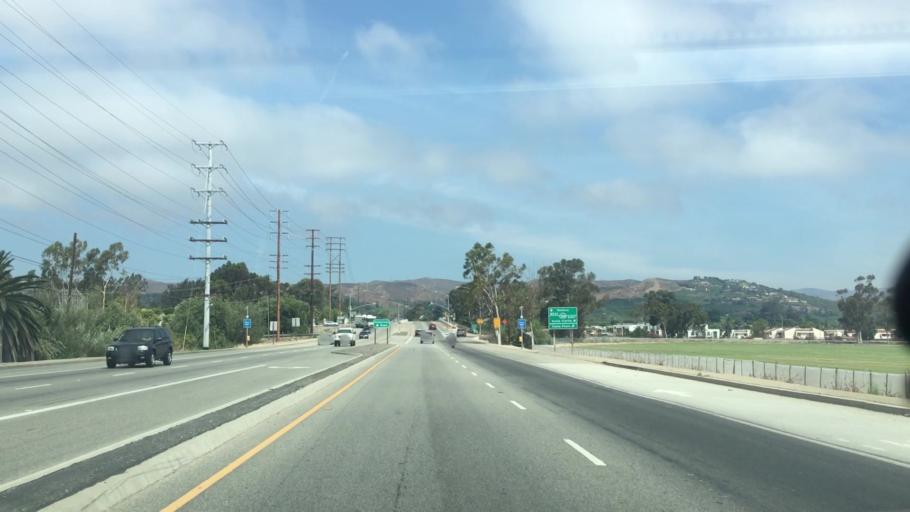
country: US
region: California
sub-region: Ventura County
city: Saticoy
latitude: 34.2869
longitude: -119.1539
